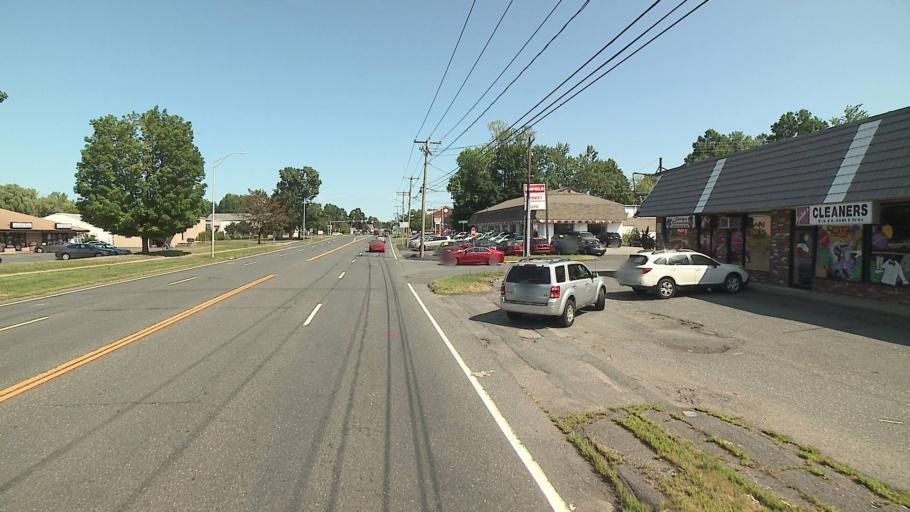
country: US
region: Connecticut
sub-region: Hartford County
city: Thompsonville
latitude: 41.9969
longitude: -72.5944
